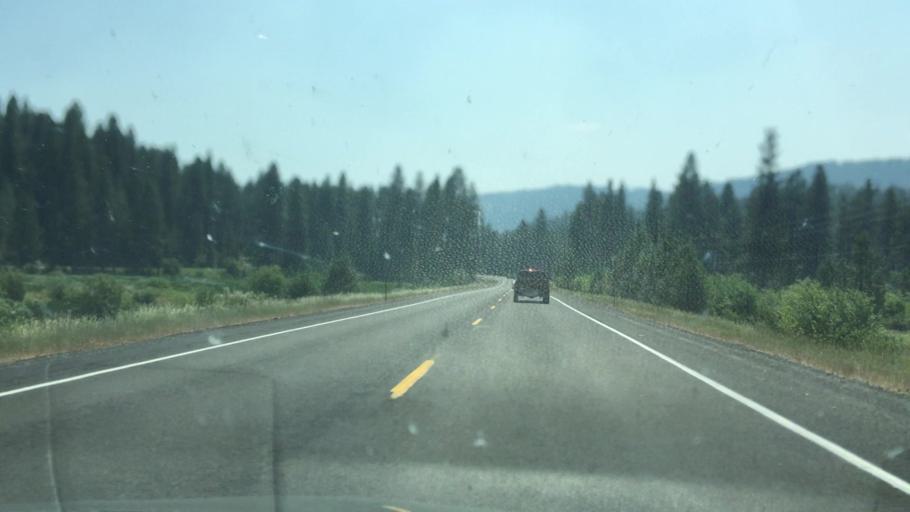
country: US
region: Idaho
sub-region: Valley County
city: McCall
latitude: 45.1020
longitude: -116.3055
